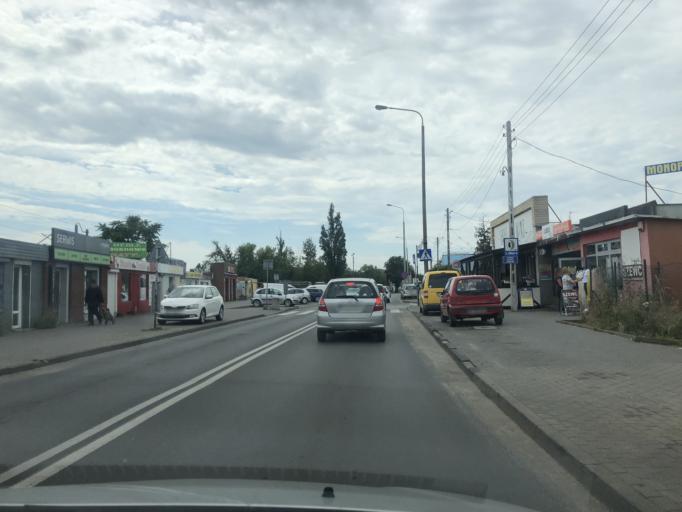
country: PL
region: Greater Poland Voivodeship
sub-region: Powiat poznanski
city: Lubon
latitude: 52.3718
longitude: 16.9022
